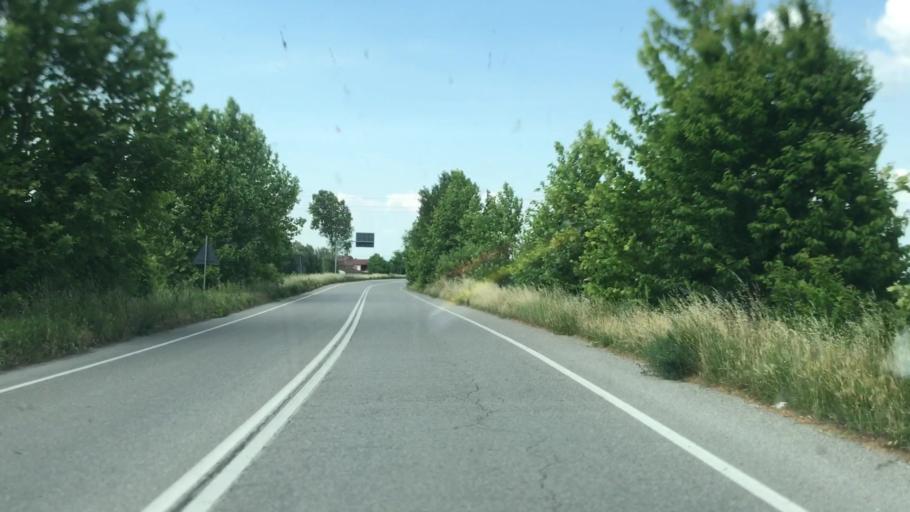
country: IT
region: Lombardy
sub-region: Provincia di Mantova
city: Castel Goffredo
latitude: 45.2956
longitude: 10.4906
